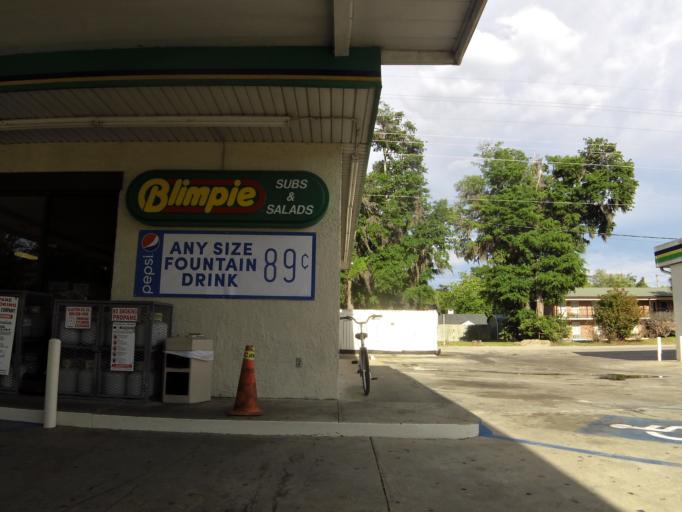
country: US
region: South Carolina
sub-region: Hampton County
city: Estill
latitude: 32.7593
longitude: -81.2409
